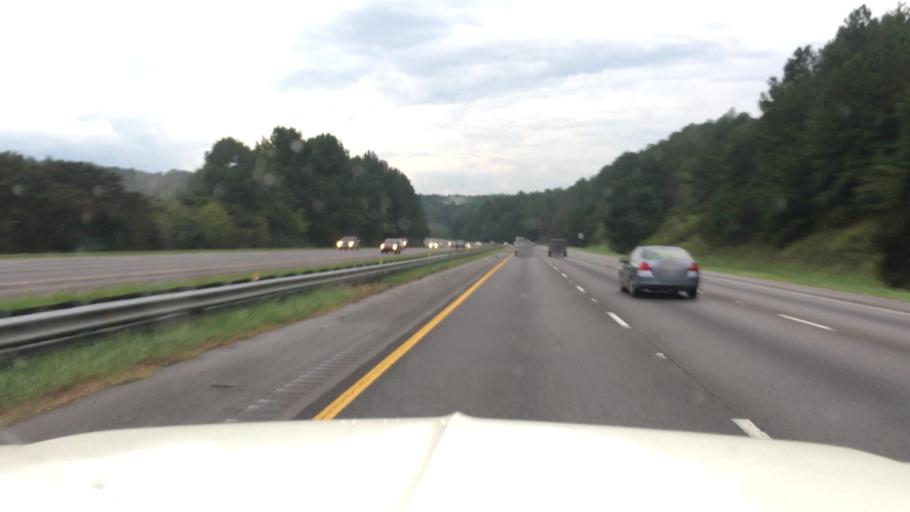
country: US
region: Alabama
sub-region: Jefferson County
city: Morris
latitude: 33.7113
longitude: -86.8337
